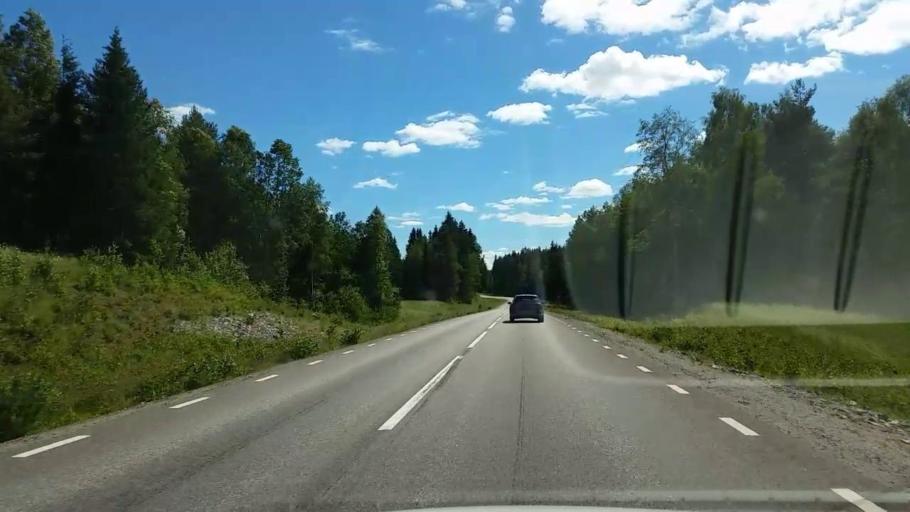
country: SE
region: Gaevleborg
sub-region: Ovanakers Kommun
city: Edsbyn
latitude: 61.1980
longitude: 15.8738
